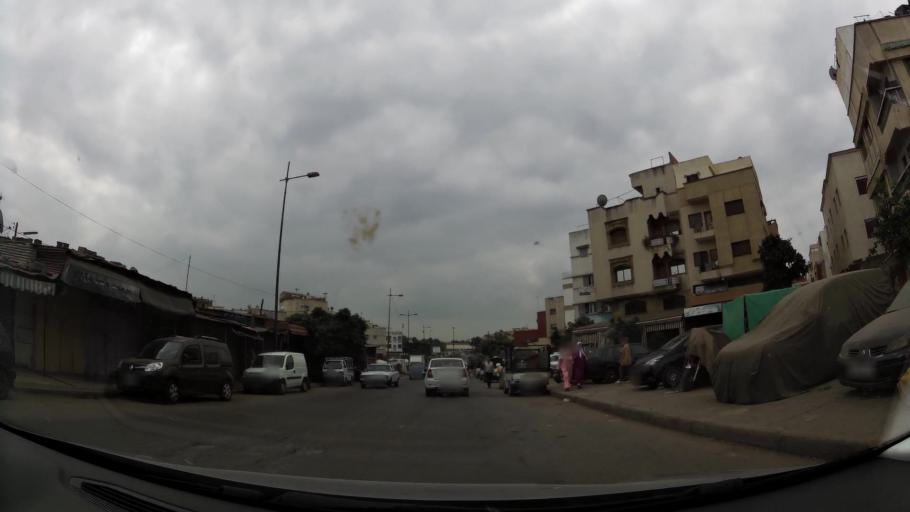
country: MA
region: Rabat-Sale-Zemmour-Zaer
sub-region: Rabat
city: Rabat
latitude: 33.9932
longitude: -6.8718
